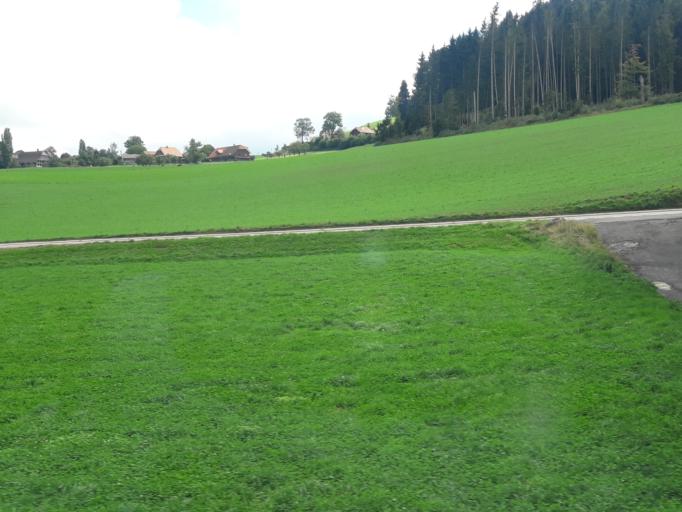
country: CH
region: Bern
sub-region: Bern-Mittelland District
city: Wahlern
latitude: 46.8395
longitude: 7.3452
